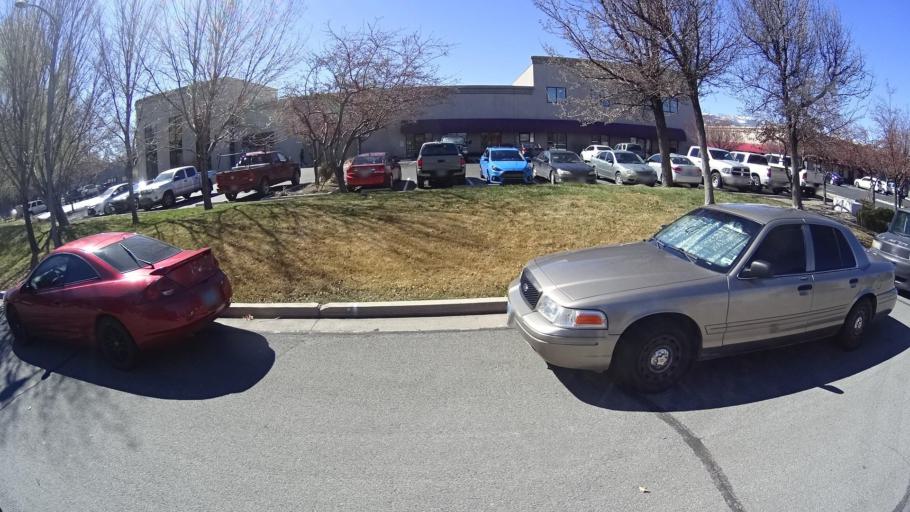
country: US
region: Nevada
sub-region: Washoe County
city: Sparks
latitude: 39.4891
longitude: -119.7600
